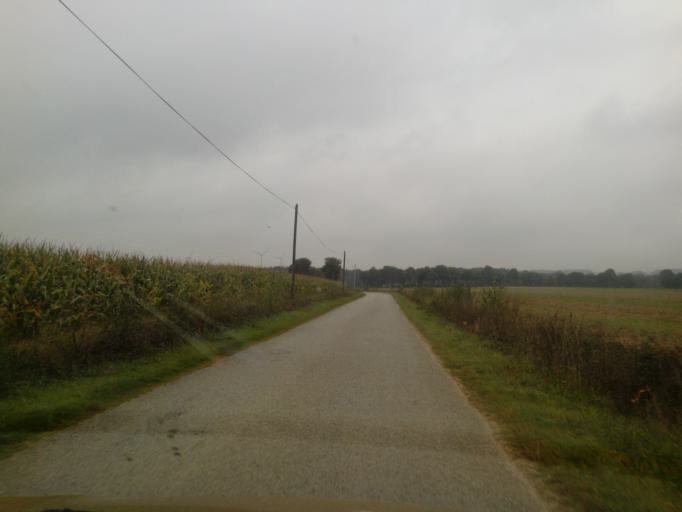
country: FR
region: Brittany
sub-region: Departement du Morbihan
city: Meneac
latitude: 48.1200
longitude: -2.4197
